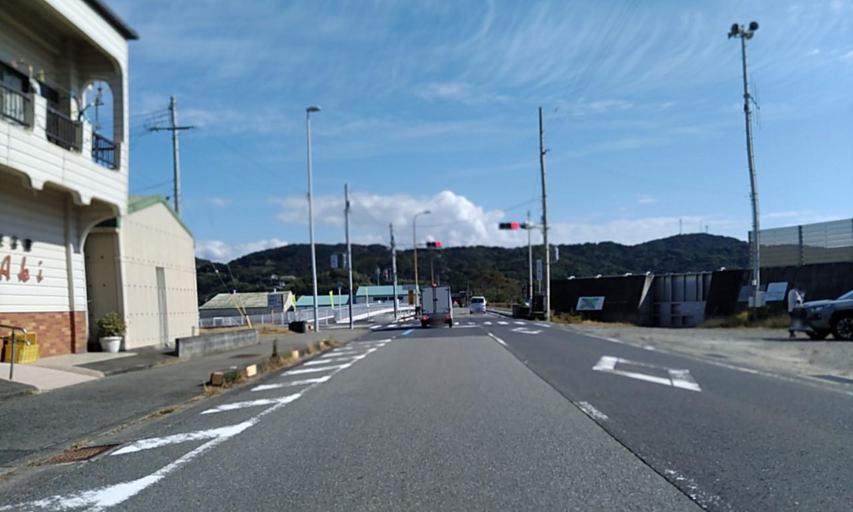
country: JP
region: Wakayama
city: Gobo
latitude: 33.7999
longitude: 135.2350
